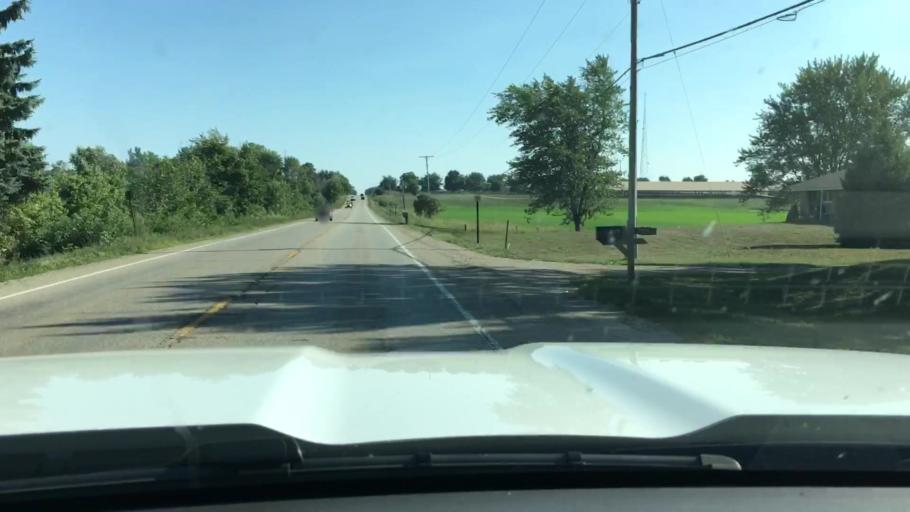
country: US
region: Michigan
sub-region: Ottawa County
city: Allendale
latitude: 43.0121
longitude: -85.9554
